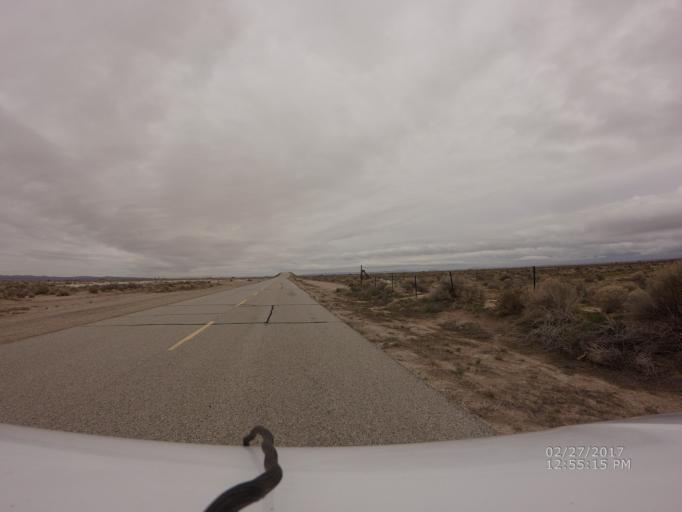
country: US
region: California
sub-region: Kern County
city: Rosamond
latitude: 34.8060
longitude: -118.1760
